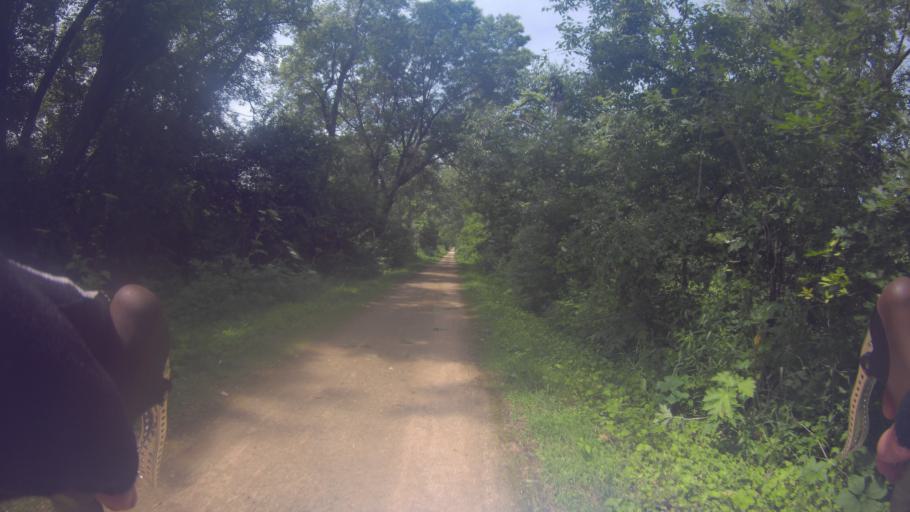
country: US
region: Wisconsin
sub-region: Dane County
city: Mount Horeb
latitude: 43.0208
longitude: -89.6766
